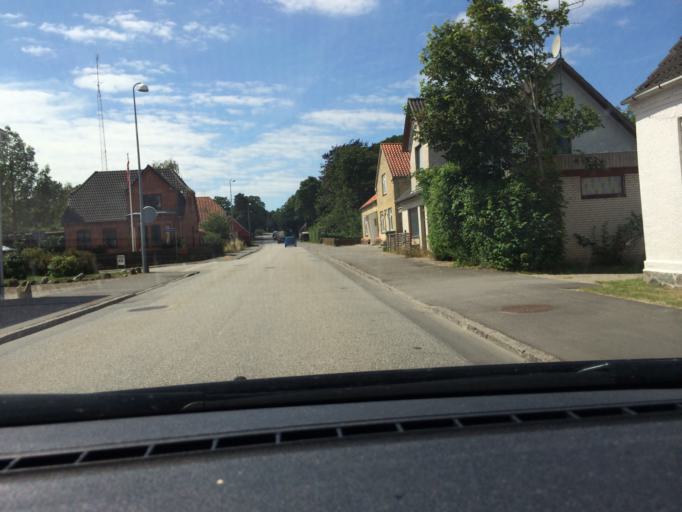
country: DK
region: Zealand
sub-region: Vordingborg Kommune
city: Stege
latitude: 54.9954
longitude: 12.4411
